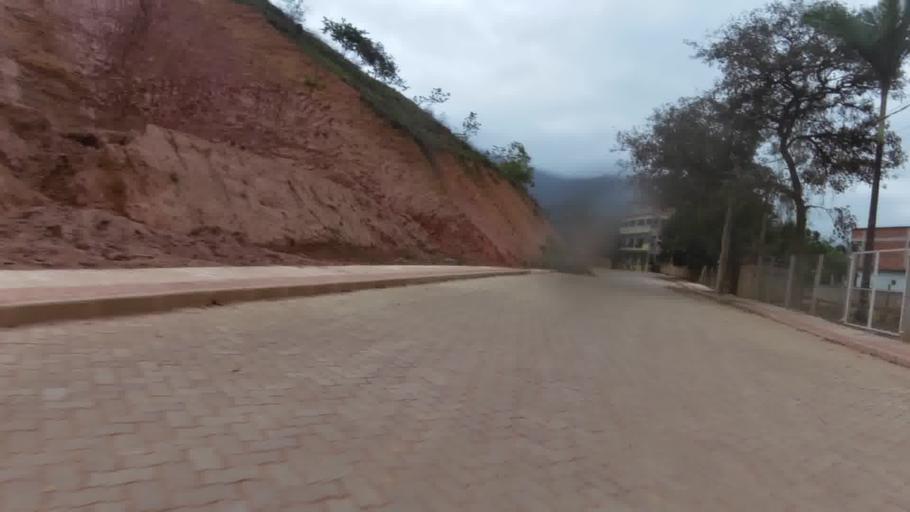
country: BR
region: Espirito Santo
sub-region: Alfredo Chaves
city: Alfredo Chaves
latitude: -20.6428
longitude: -40.7434
